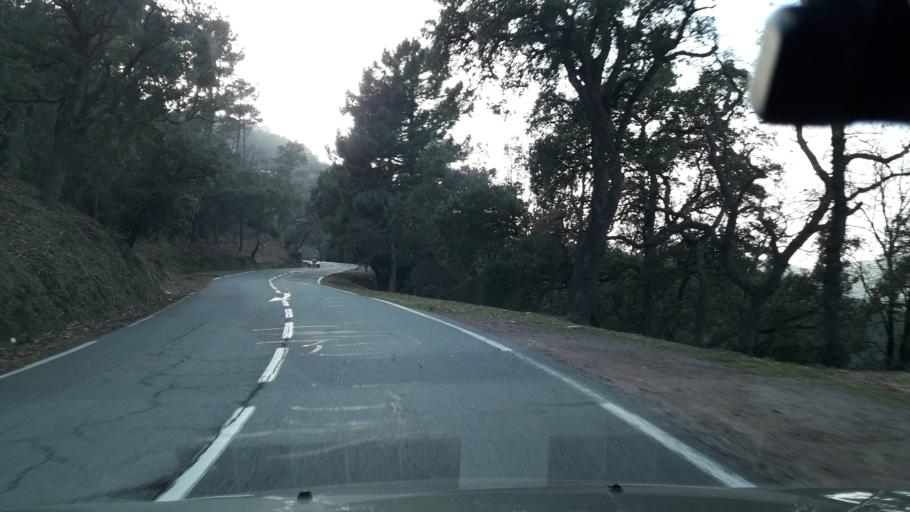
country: FR
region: Provence-Alpes-Cote d'Azur
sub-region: Departement du Var
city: Tanneron
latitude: 43.5185
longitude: 6.8568
